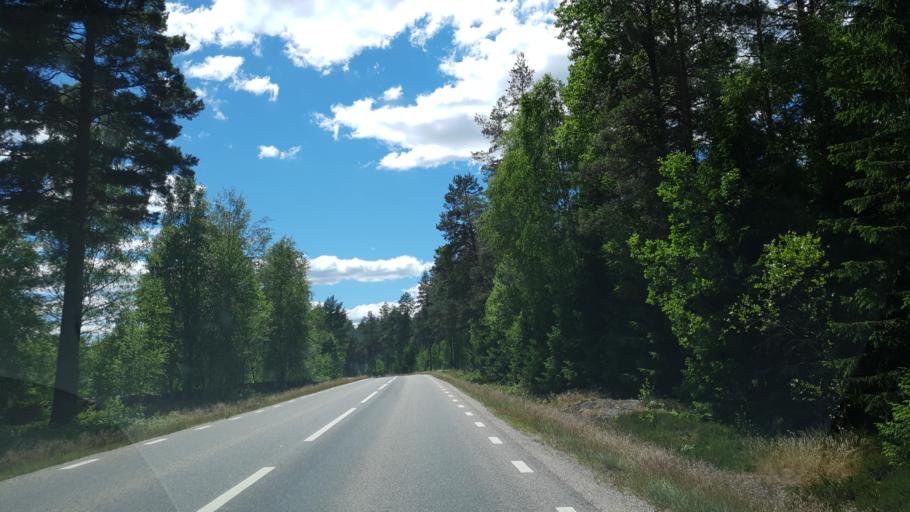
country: SE
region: Kronoberg
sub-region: Lessebo Kommun
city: Lessebo
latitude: 56.7959
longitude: 15.3176
